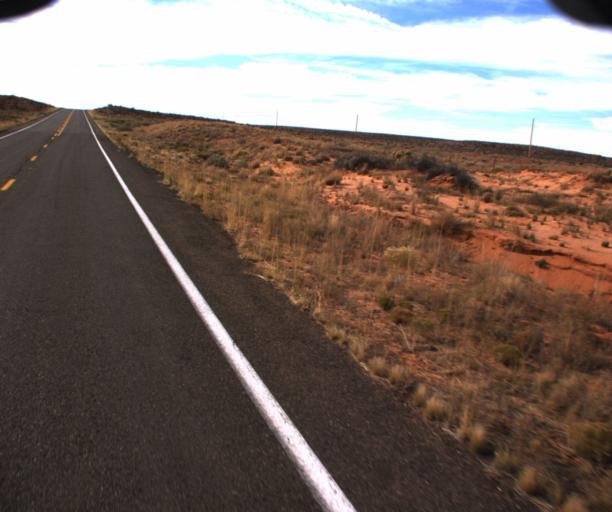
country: US
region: Arizona
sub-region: Coconino County
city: LeChee
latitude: 36.7626
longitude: -111.2852
